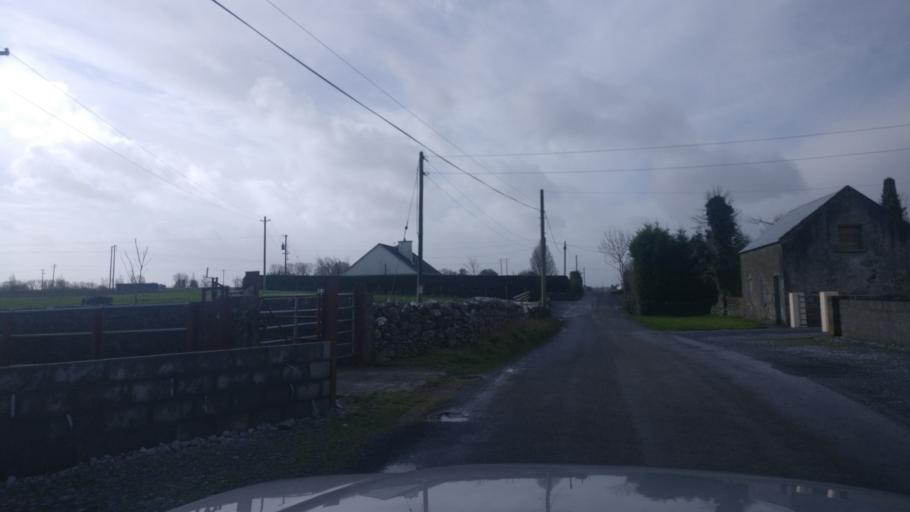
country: IE
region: Connaught
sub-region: County Galway
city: Loughrea
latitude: 53.2683
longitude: -8.5993
